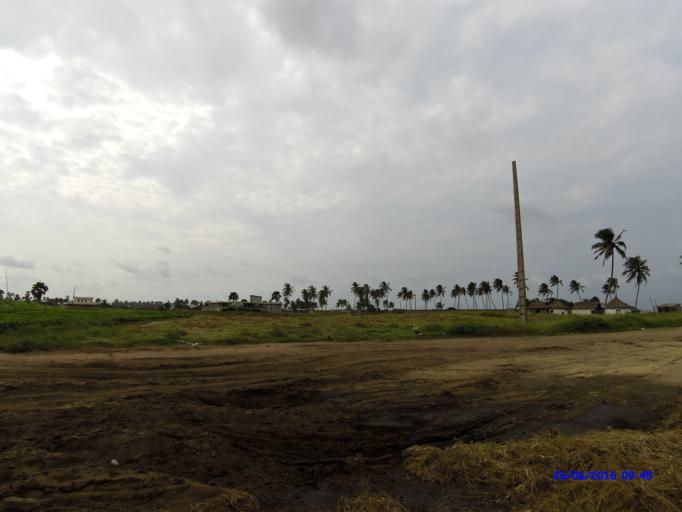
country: BJ
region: Atlantique
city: Hevie
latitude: 6.3492
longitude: 2.3081
